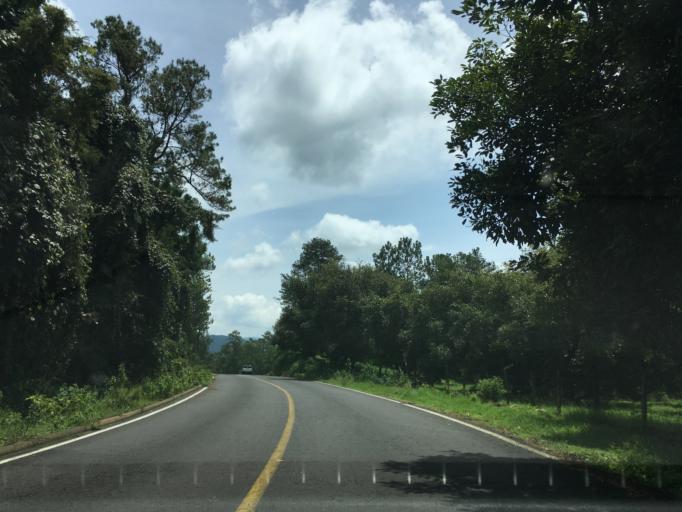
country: MX
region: Michoacan
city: Nuevo San Juan Parangaricutiro
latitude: 19.4429
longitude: -102.1641
